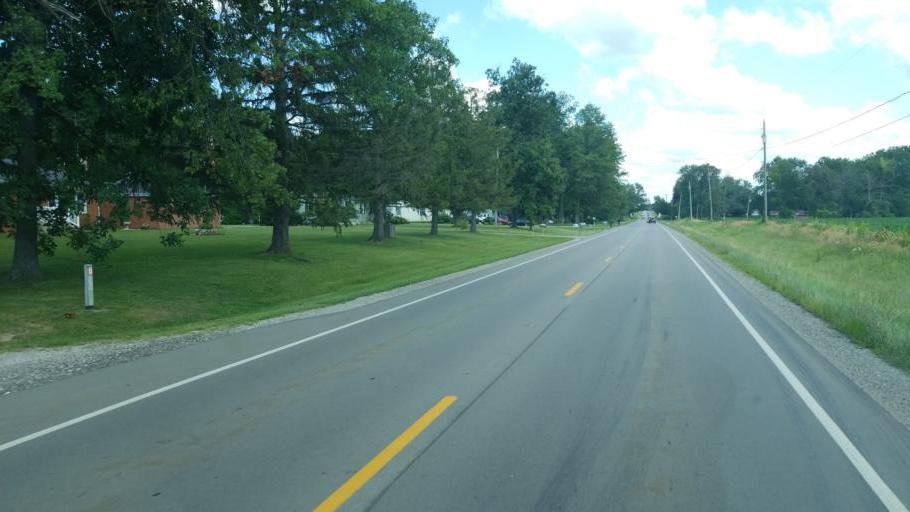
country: US
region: Ohio
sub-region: Crawford County
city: Galion
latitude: 40.6833
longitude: -82.7970
